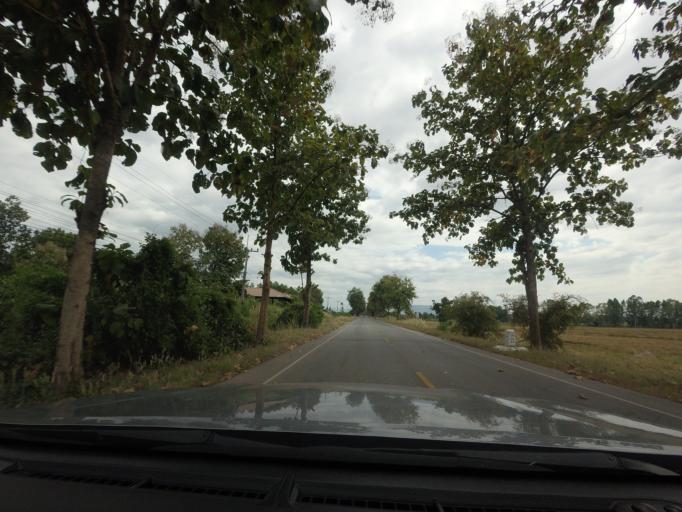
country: TH
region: Phitsanulok
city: Wang Thong
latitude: 16.7092
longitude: 100.4852
